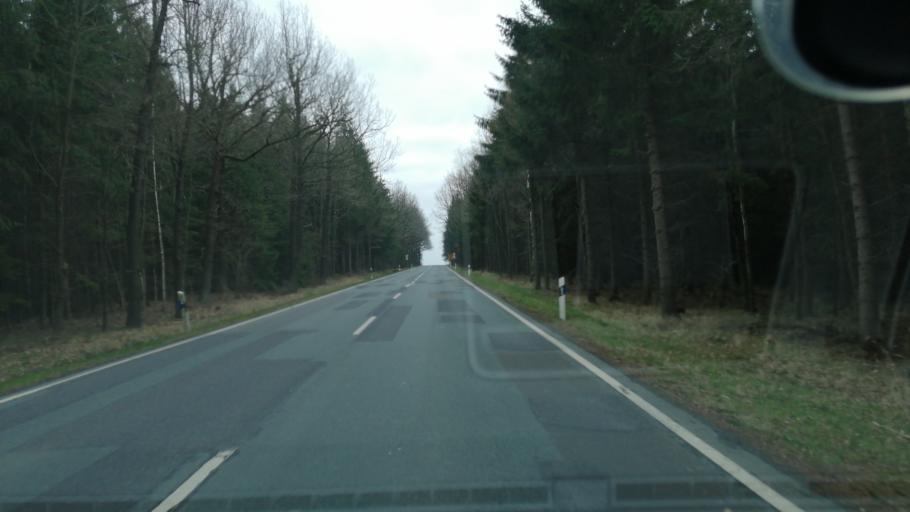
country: DE
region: Saxony
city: Niedercunnersdorf
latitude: 51.0488
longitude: 14.7029
